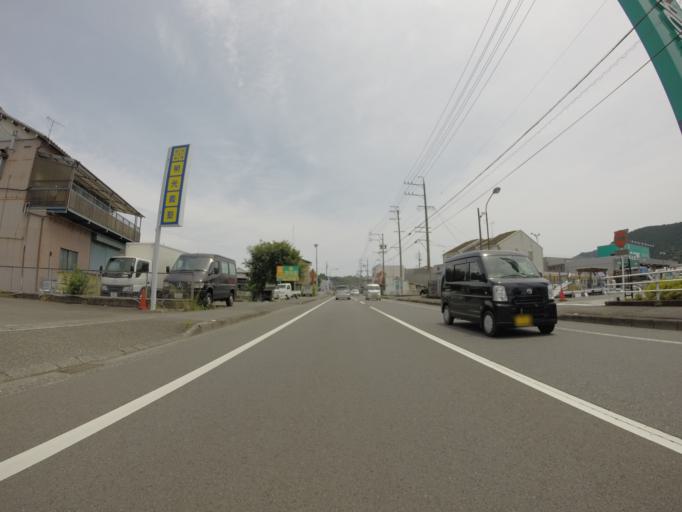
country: JP
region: Shizuoka
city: Shizuoka-shi
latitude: 34.9843
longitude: 138.3292
